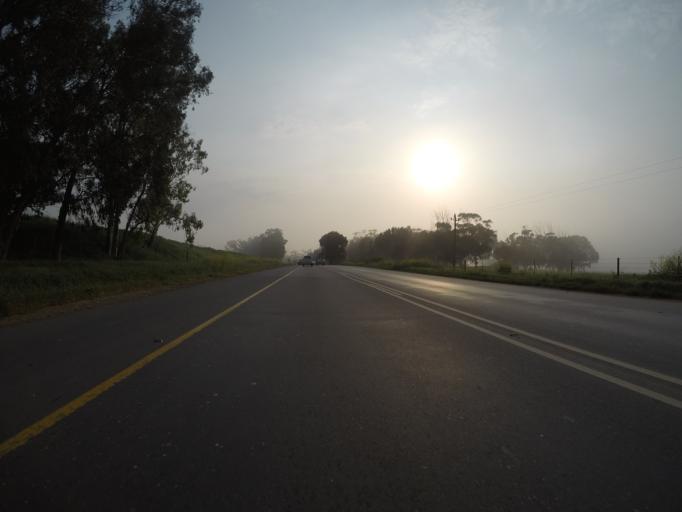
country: ZA
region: Western Cape
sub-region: City of Cape Town
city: Kraaifontein
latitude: -33.7963
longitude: 18.6920
